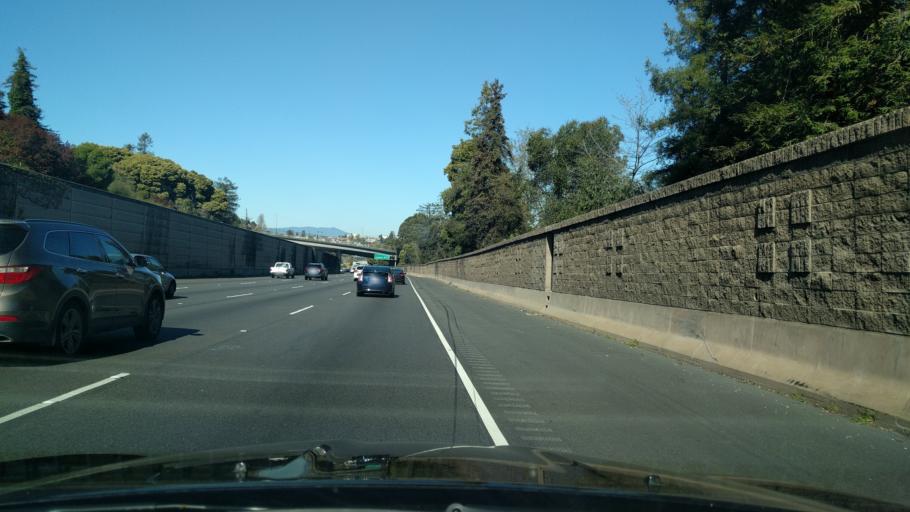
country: US
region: California
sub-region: Alameda County
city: Piedmont
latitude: 37.8073
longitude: -122.2389
